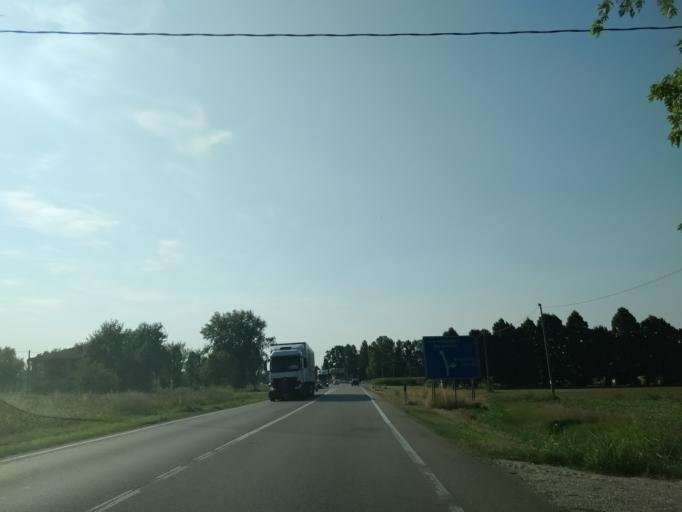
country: IT
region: Emilia-Romagna
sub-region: Provincia di Bologna
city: Argelato
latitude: 44.6046
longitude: 11.3359
